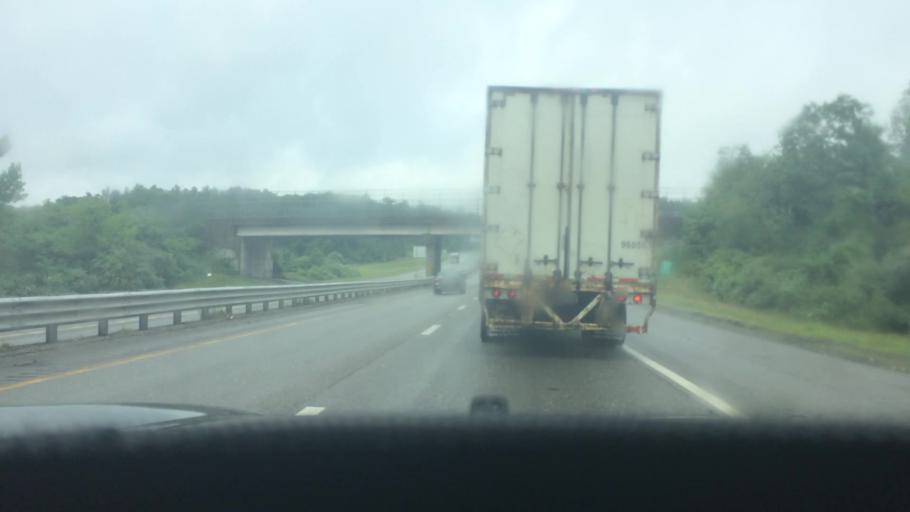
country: US
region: Massachusetts
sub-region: Worcester County
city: Westminster
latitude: 42.5430
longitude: -71.8821
